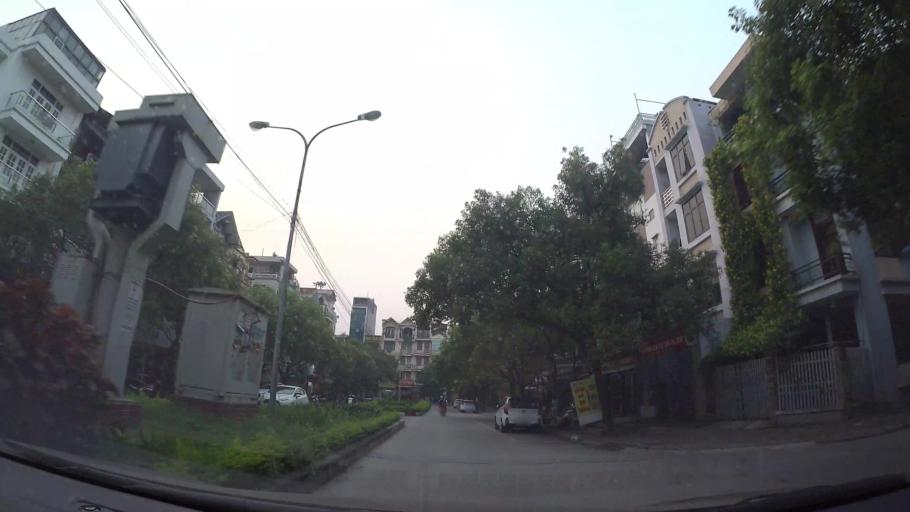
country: VN
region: Ha Noi
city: Thanh Xuan
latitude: 20.9793
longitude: 105.7949
